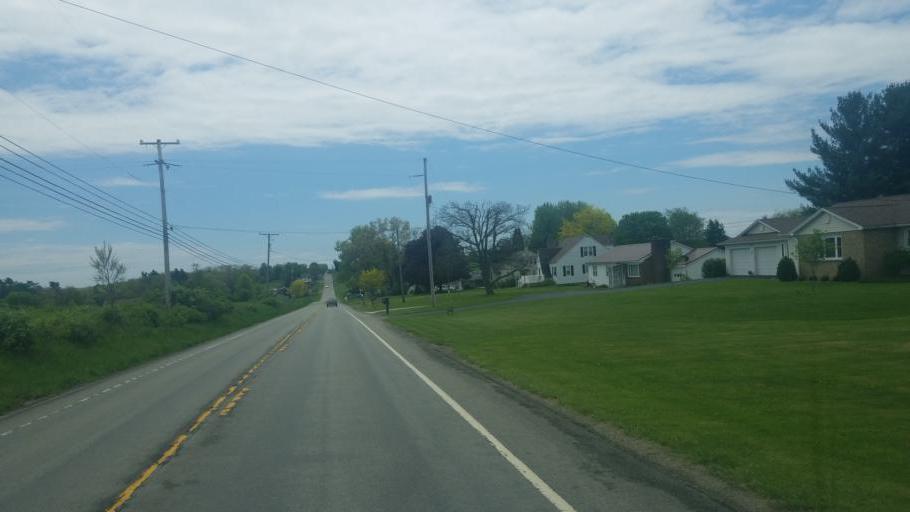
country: US
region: Pennsylvania
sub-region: Clarion County
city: Marianne
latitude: 41.2628
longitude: -79.4592
